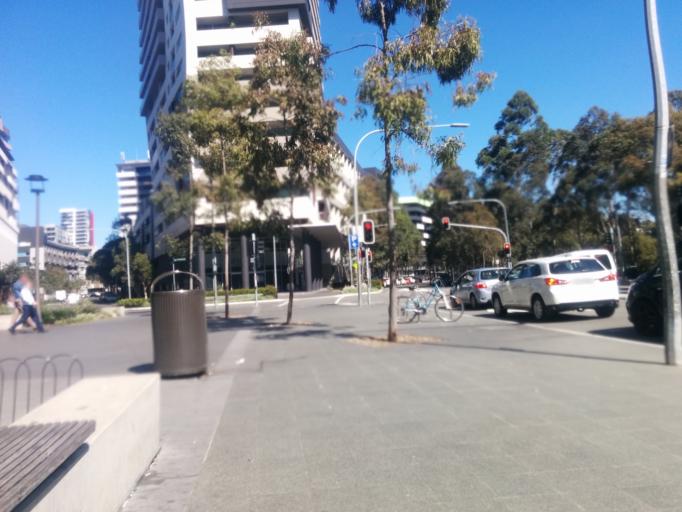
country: AU
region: New South Wales
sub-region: City of Sydney
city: Alexandria
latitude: -33.9048
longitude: 151.2124
